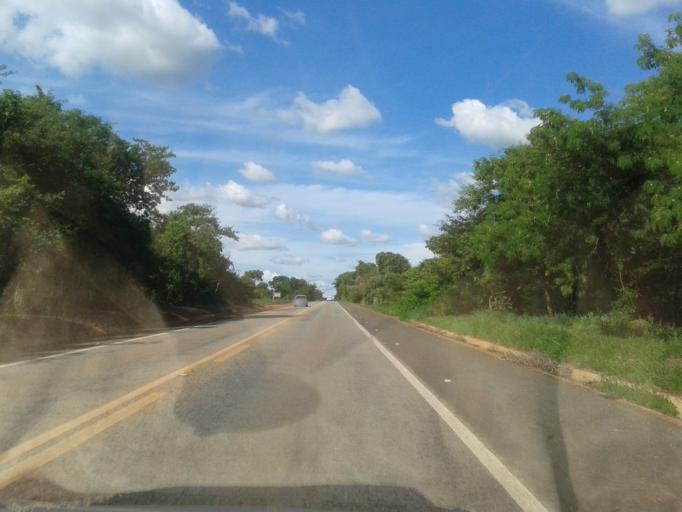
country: BR
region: Goias
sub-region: Mozarlandia
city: Mozarlandia
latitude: -15.0656
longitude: -50.6160
